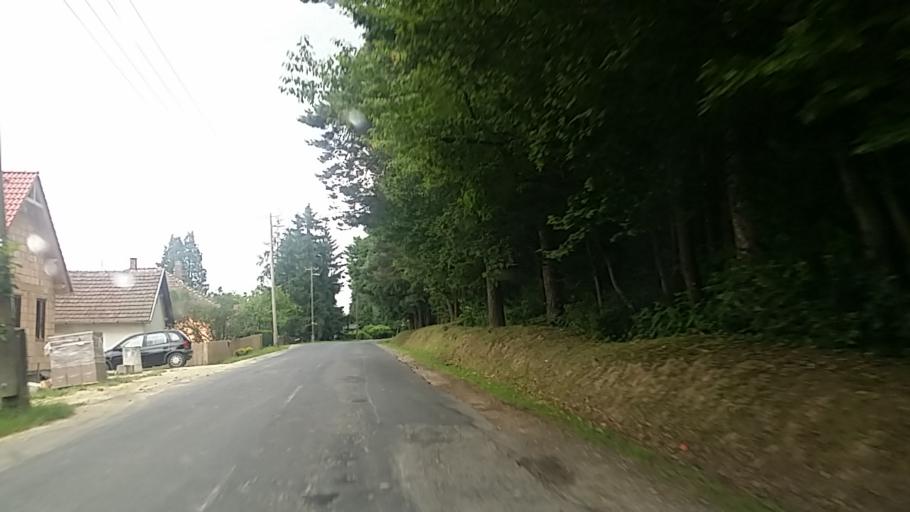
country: SI
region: Hodos-Hodos
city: Hodos
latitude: 46.8431
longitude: 16.4146
